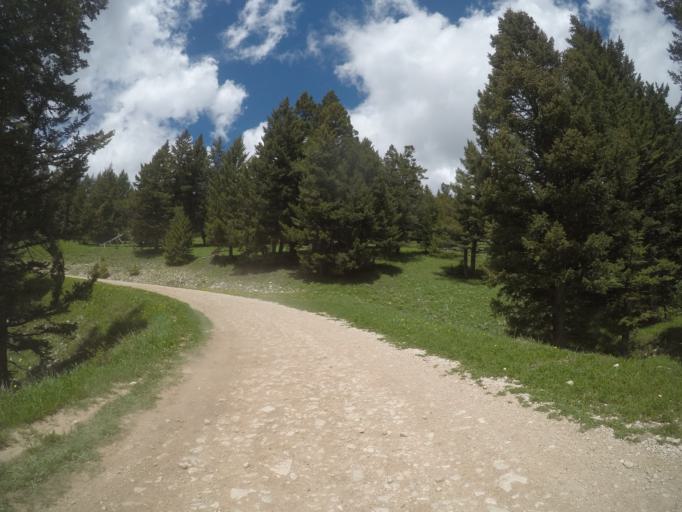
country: US
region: Wyoming
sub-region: Big Horn County
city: Lovell
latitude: 45.1672
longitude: -108.4087
